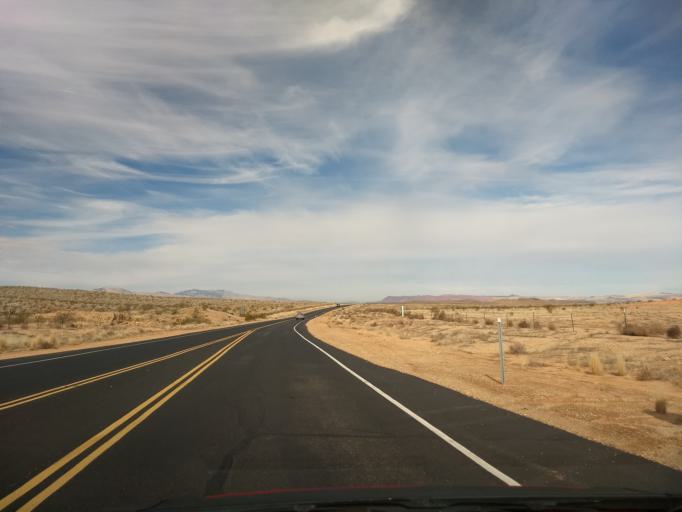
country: US
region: Utah
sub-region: Washington County
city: Washington
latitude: 37.0157
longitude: -113.4962
